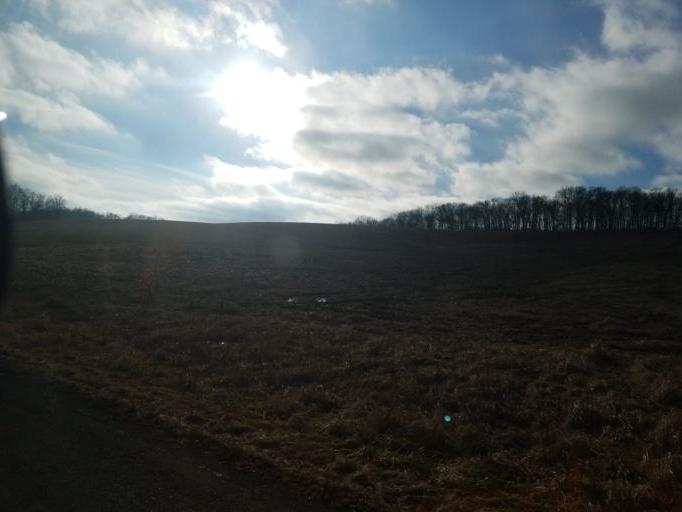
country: US
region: Ohio
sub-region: Ashland County
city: Loudonville
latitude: 40.5910
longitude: -82.3570
